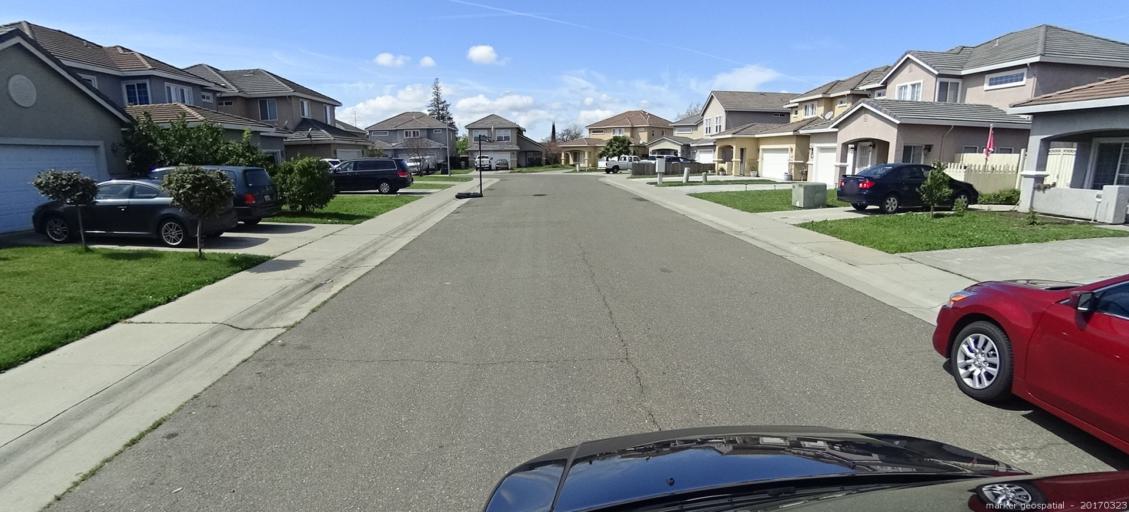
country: US
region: California
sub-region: Sacramento County
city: Florin
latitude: 38.5098
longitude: -121.4199
